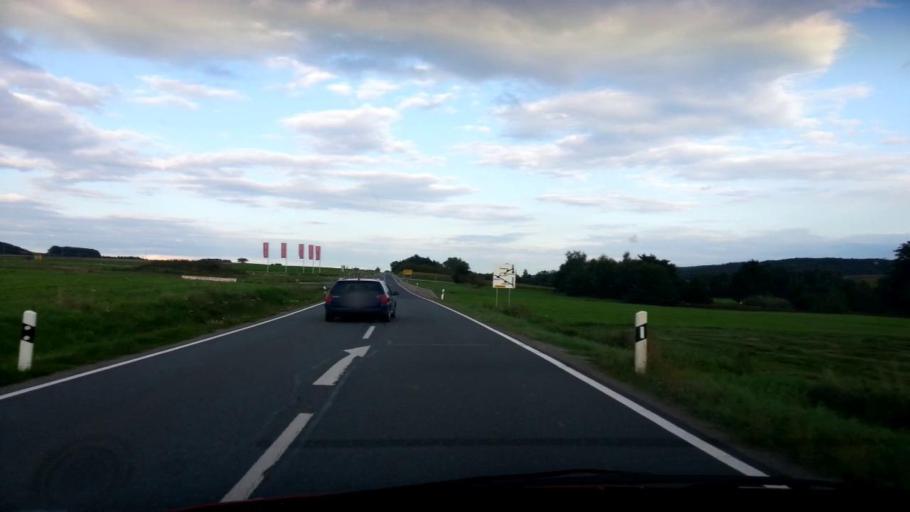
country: DE
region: Bavaria
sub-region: Regierungsbezirk Unterfranken
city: Geiselwind
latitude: 49.7710
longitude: 10.4937
